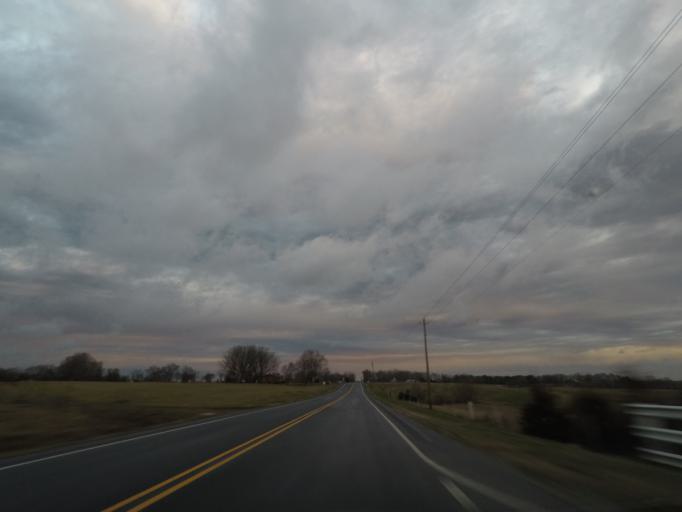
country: US
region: North Carolina
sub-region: Caswell County
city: Yanceyville
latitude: 36.3676
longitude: -79.2553
